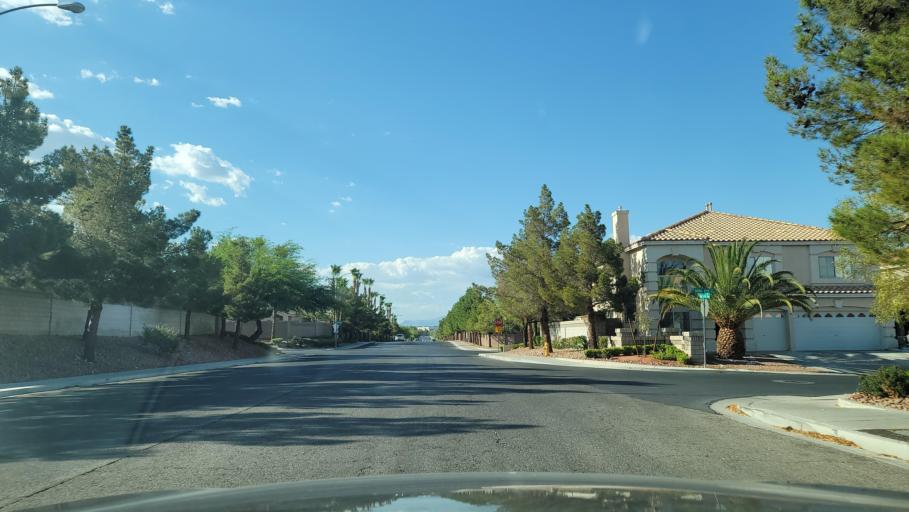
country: US
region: Nevada
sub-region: Clark County
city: Summerlin South
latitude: 36.0956
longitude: -115.3019
